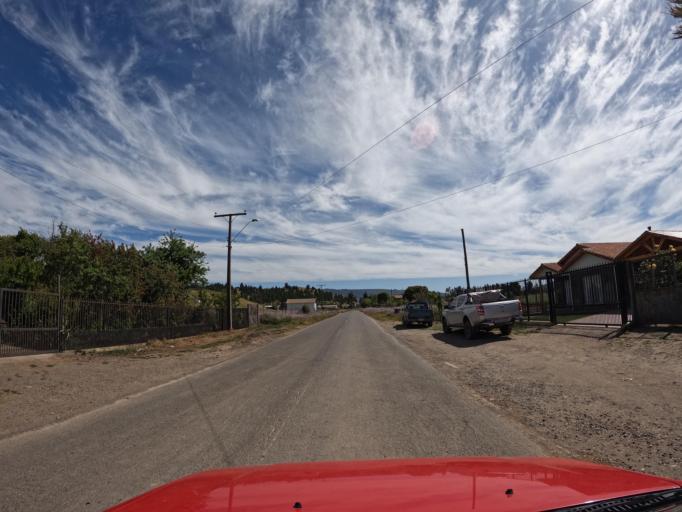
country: CL
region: Maule
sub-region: Provincia de Talca
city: Constitucion
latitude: -35.0266
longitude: -72.0466
